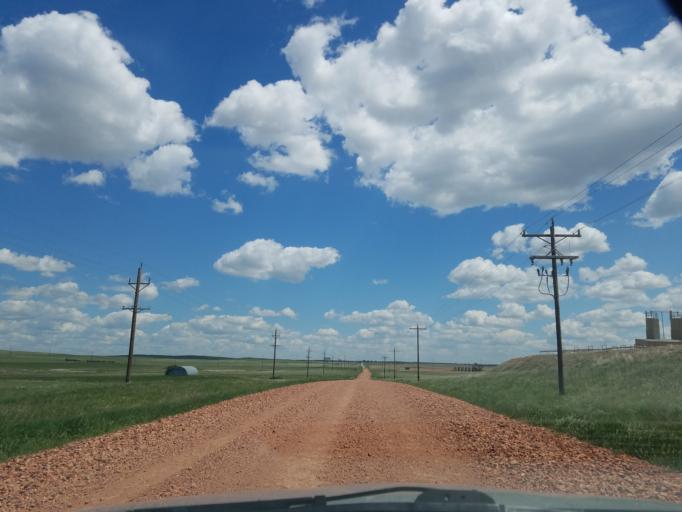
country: US
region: North Dakota
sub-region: McKenzie County
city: Watford City
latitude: 47.8194
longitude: -103.5967
